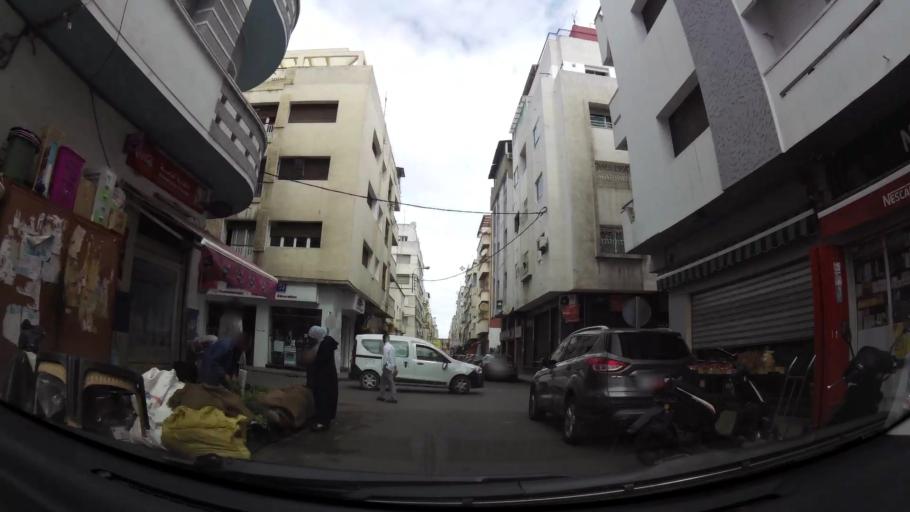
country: MA
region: Grand Casablanca
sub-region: Casablanca
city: Casablanca
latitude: 33.5813
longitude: -7.6364
